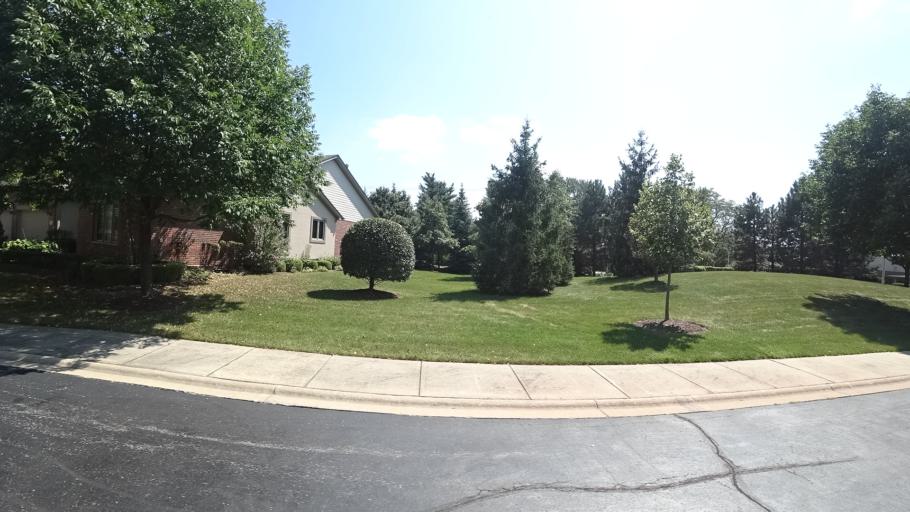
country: US
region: Illinois
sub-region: Cook County
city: Orland Park
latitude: 41.6314
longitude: -87.8340
